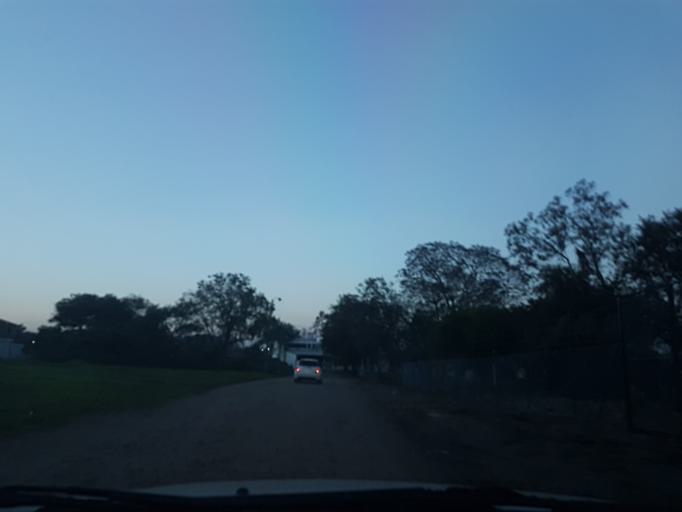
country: PY
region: Central
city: Colonia Mariano Roque Alonso
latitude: -25.2289
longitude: -57.5292
